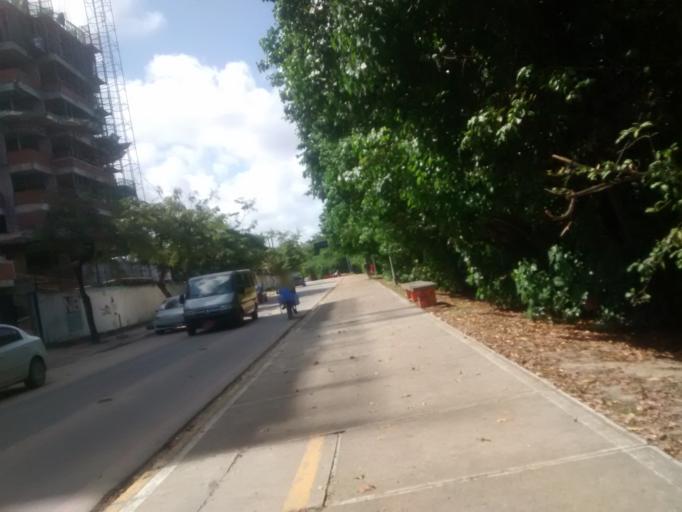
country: BR
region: Pernambuco
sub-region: Recife
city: Recife
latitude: -8.0951
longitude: -34.9167
